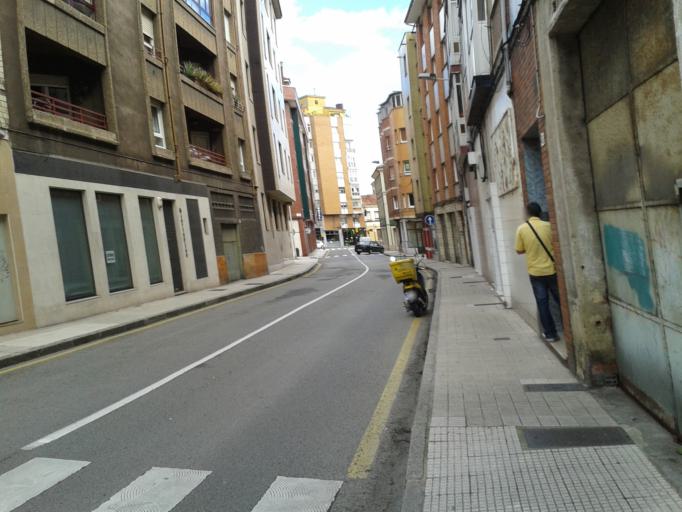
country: ES
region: Asturias
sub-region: Province of Asturias
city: Natahoyo
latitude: 43.5397
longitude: -5.6832
